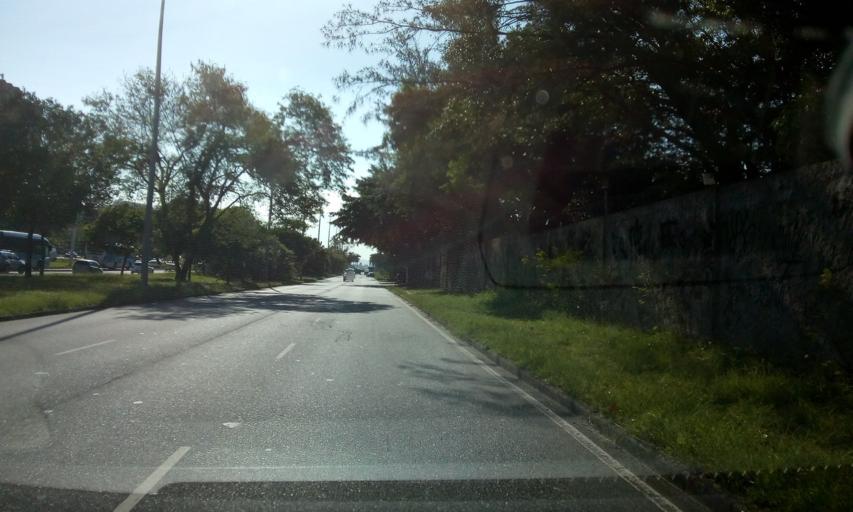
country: BR
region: Rio de Janeiro
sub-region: Nilopolis
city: Nilopolis
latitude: -23.0000
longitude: -43.3919
